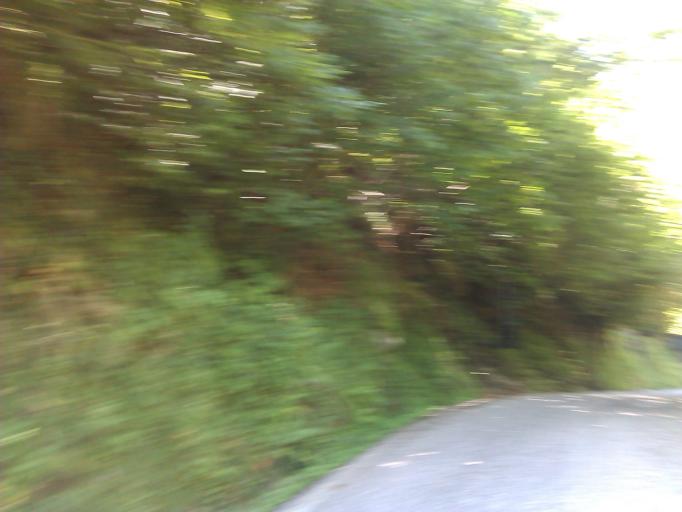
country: IT
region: Tuscany
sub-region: Provincia di Prato
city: Cantagallo
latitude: 44.0294
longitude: 11.0386
